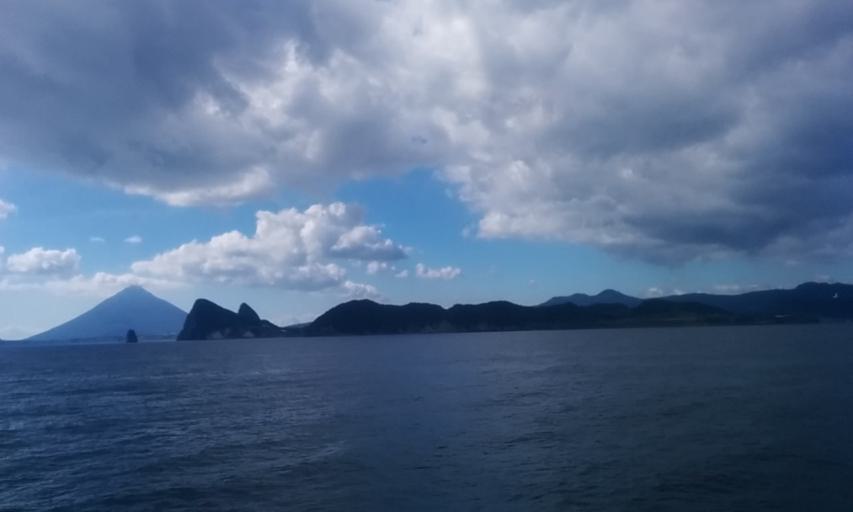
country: JP
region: Kagoshima
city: Ibusuki
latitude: 31.1792
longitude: 130.6669
